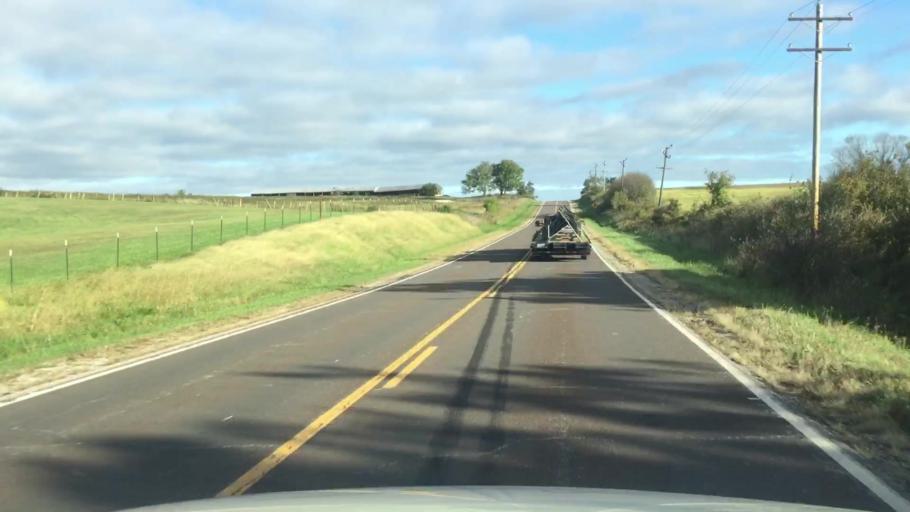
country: US
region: Missouri
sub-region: Howard County
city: New Franklin
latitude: 39.0724
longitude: -92.7458
